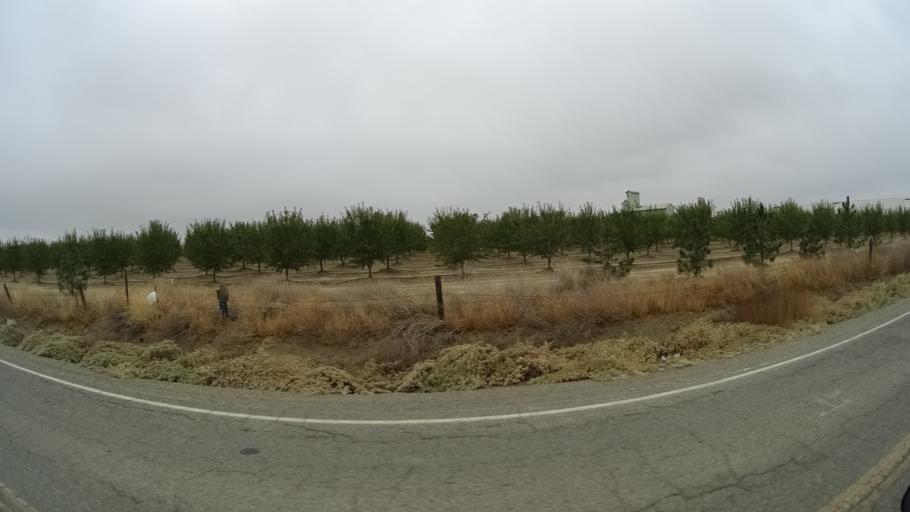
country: US
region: California
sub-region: Yolo County
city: Dunnigan
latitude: 38.9255
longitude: -121.9941
